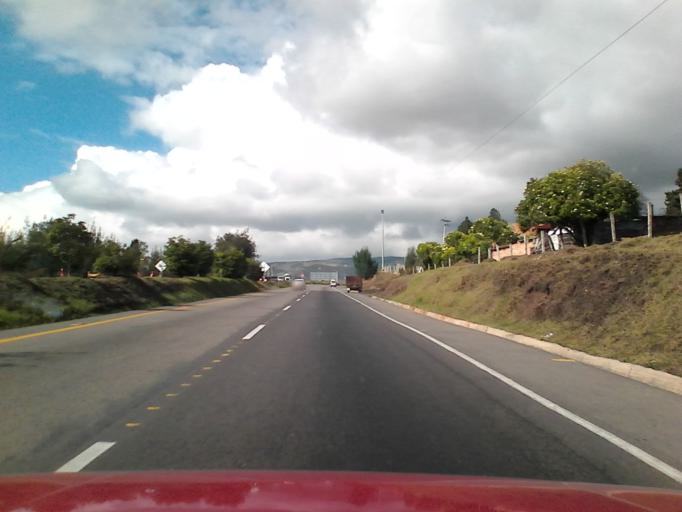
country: CO
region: Boyaca
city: Combita
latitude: 5.6294
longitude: -73.3007
